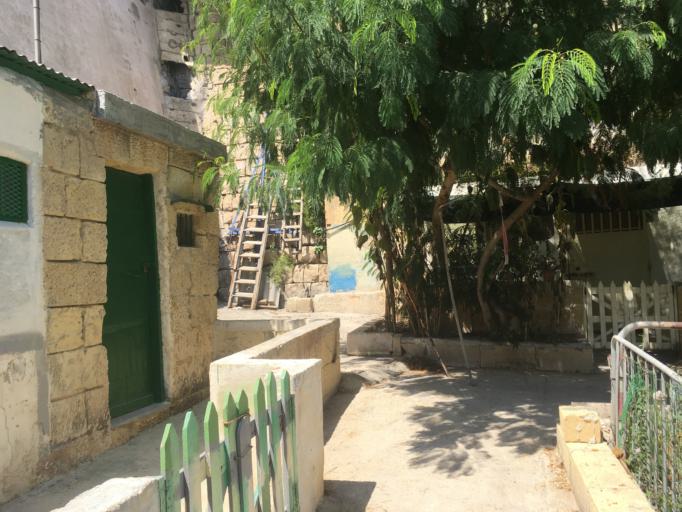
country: MT
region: Il-Belt Valletta
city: Valletta
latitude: 35.8983
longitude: 14.5182
